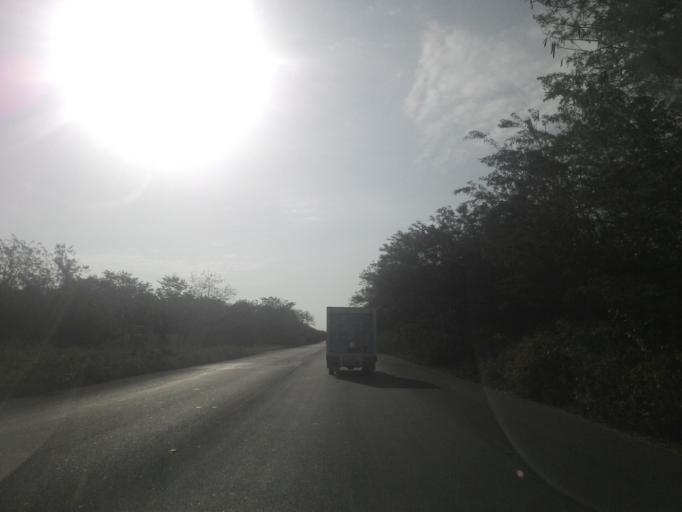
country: MX
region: Yucatan
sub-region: Valladolid
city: Tesoco
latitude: 20.7141
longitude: -88.1687
